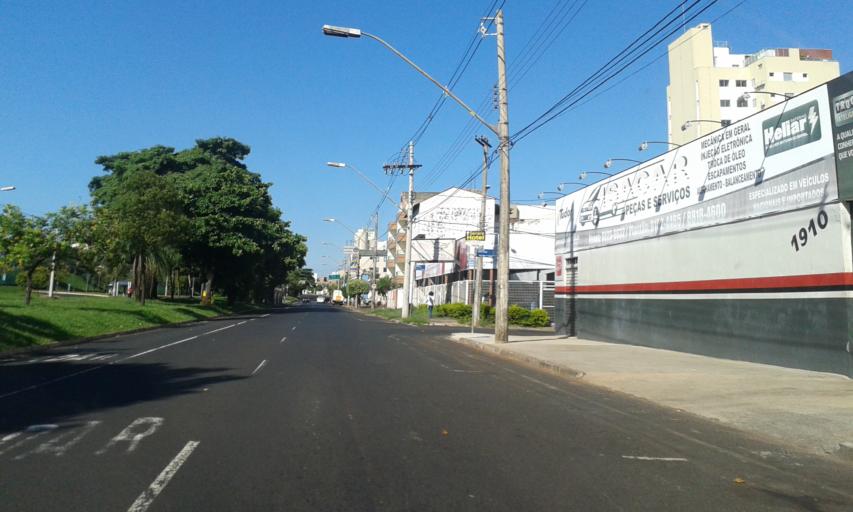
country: BR
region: Minas Gerais
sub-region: Uberlandia
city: Uberlandia
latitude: -18.9165
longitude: -48.2598
